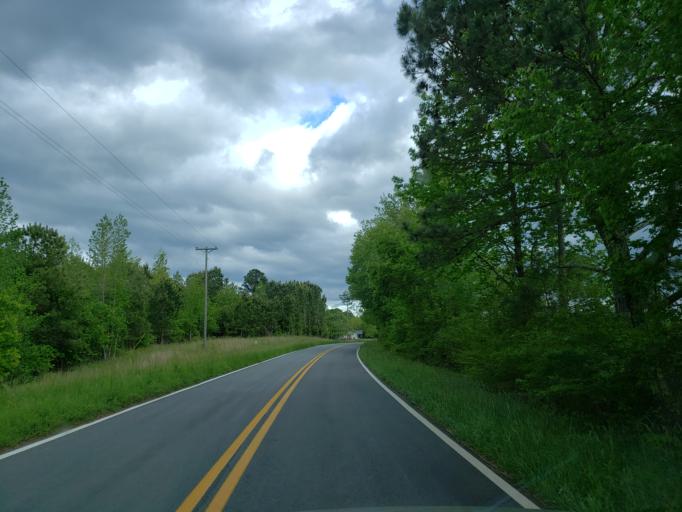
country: US
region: Georgia
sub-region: Haralson County
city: Tallapoosa
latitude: 33.8668
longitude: -85.3130
